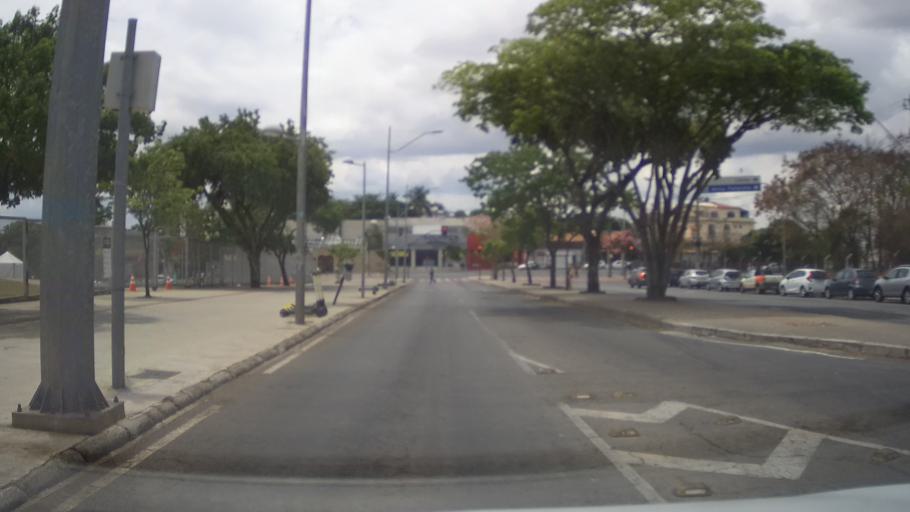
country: BR
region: Minas Gerais
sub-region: Belo Horizonte
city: Belo Horizonte
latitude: -19.8641
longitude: -43.9701
